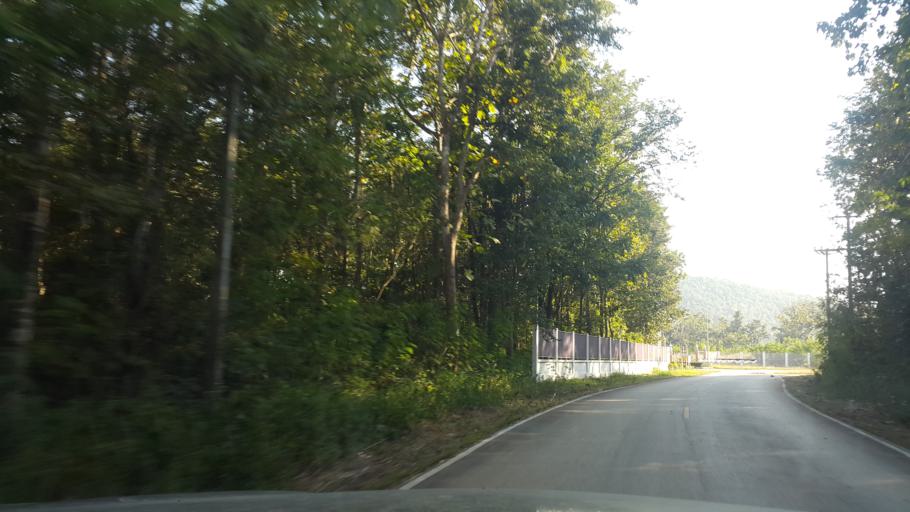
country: TH
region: Lamphun
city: Mae Tha
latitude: 18.5128
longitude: 99.1105
